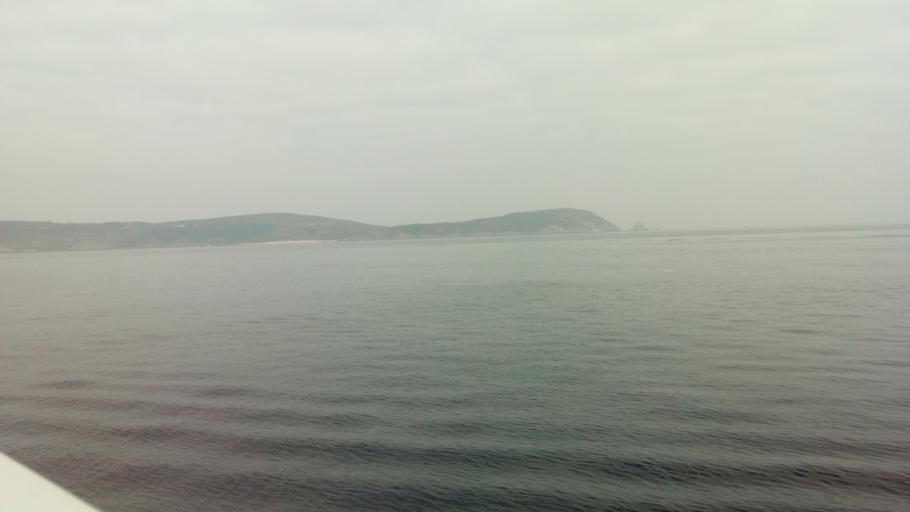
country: ES
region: Galicia
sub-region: Provincia de Pontevedra
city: Sanxenxo
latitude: 42.3793
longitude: -8.9015
